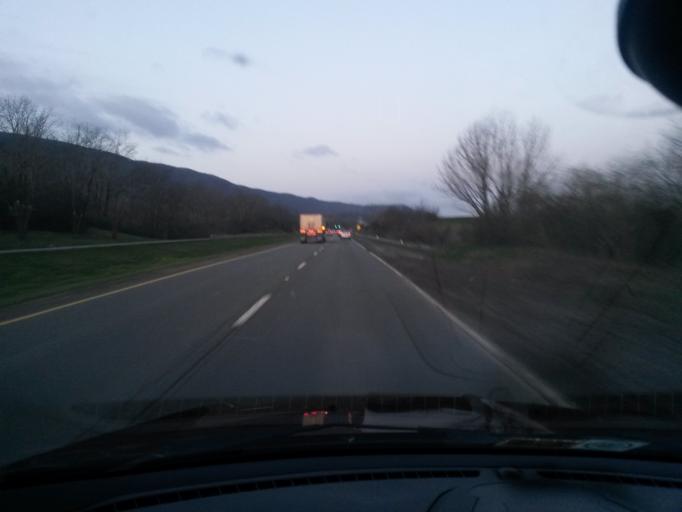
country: US
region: Virginia
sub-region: Tazewell County
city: Bluefield
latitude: 37.2404
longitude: -81.2435
